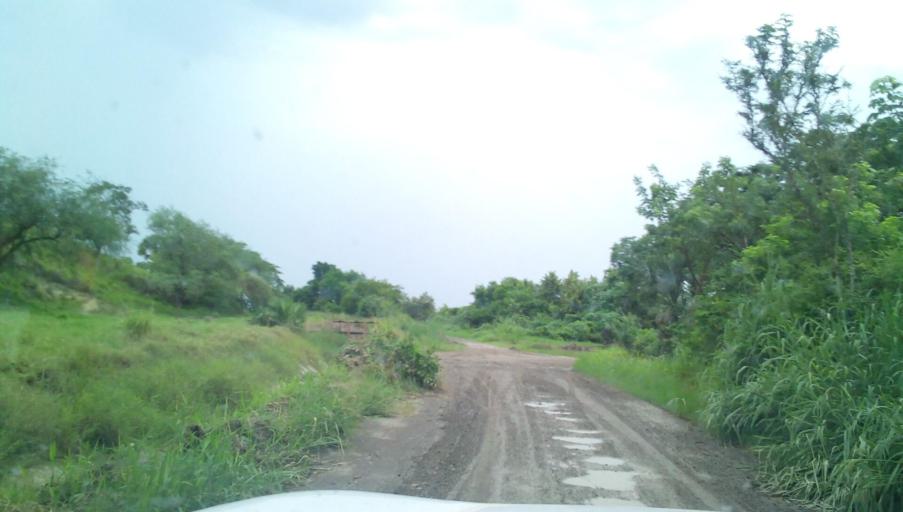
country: MX
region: Veracruz
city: Panuco
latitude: 21.8122
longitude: -98.1122
